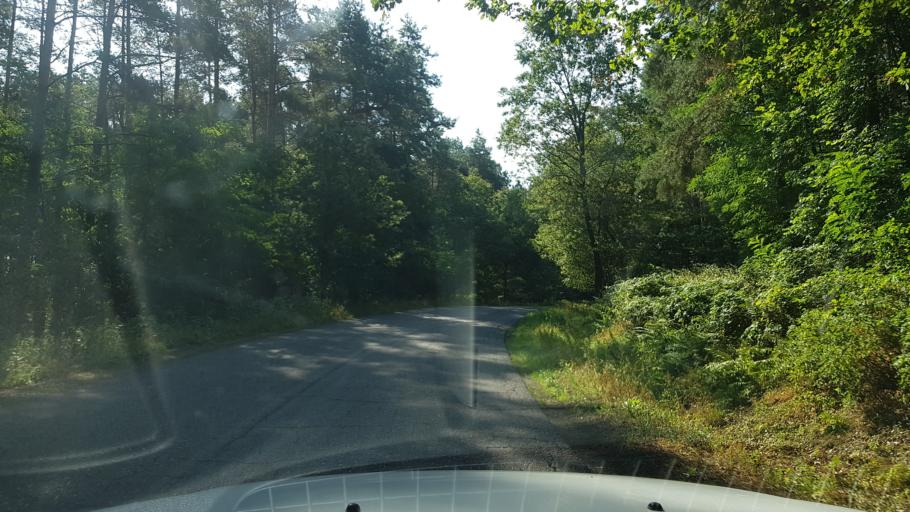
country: PL
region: West Pomeranian Voivodeship
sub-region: Powiat stargardzki
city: Dolice
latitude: 53.2239
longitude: 15.2141
